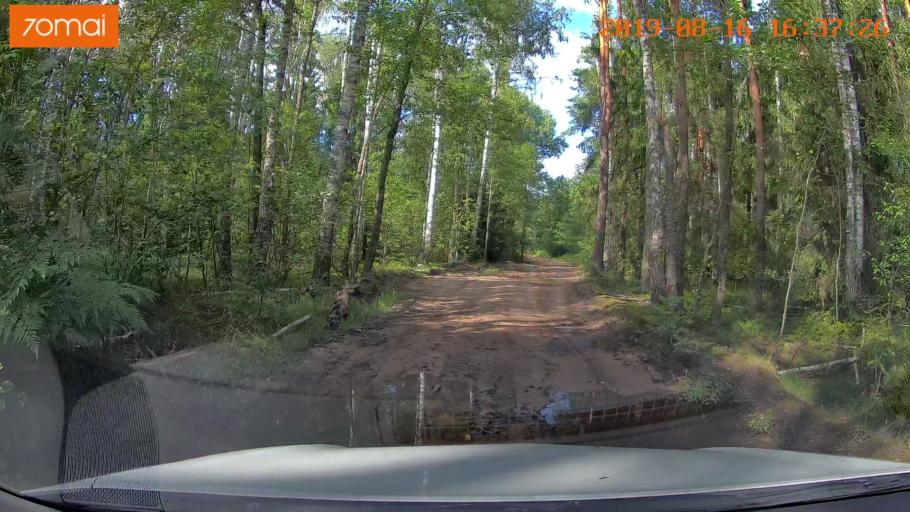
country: BY
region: Mogilev
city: Asipovichy
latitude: 53.2323
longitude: 28.7765
